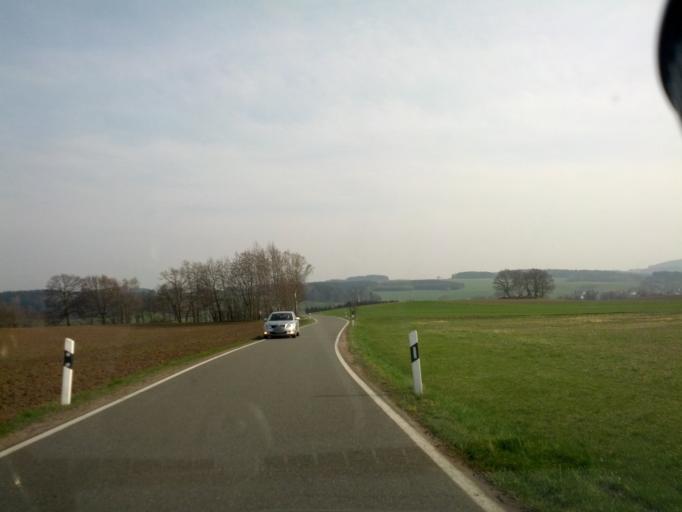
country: DE
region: Saxony
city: Stutzengrun
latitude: 50.5750
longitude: 12.5251
